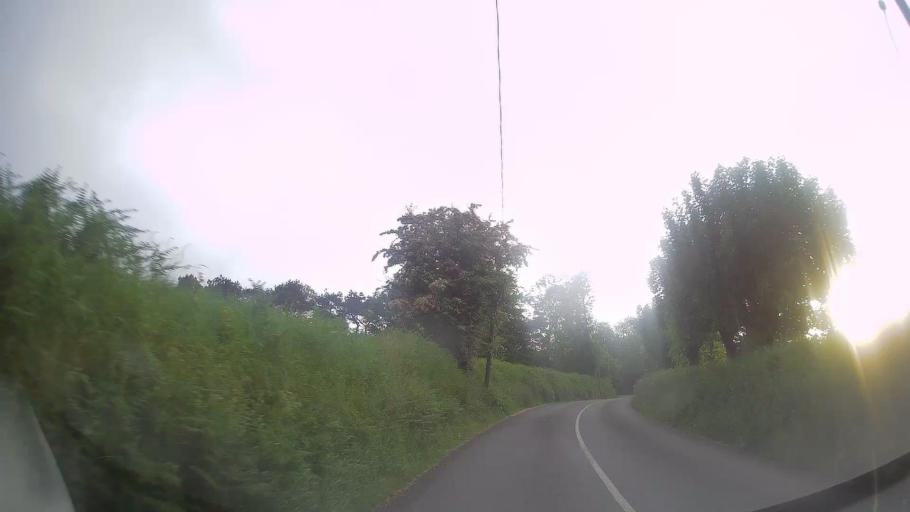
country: IE
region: Munster
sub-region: County Cork
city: Blarney
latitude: 51.9786
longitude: -8.5439
